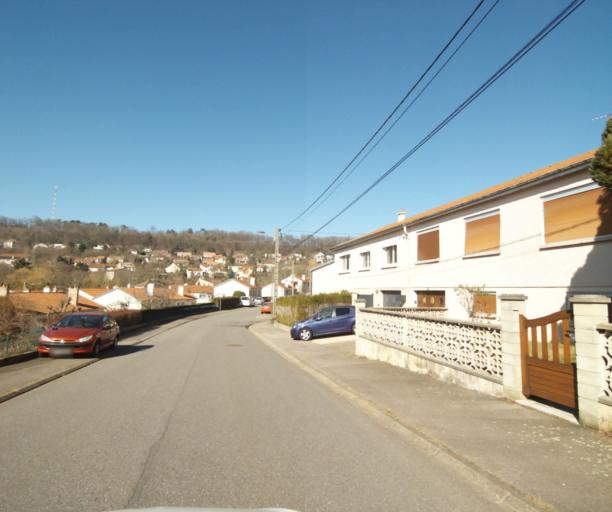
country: FR
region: Lorraine
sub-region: Departement de Meurthe-et-Moselle
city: Essey-les-Nancy
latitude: 48.7123
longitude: 6.2197
